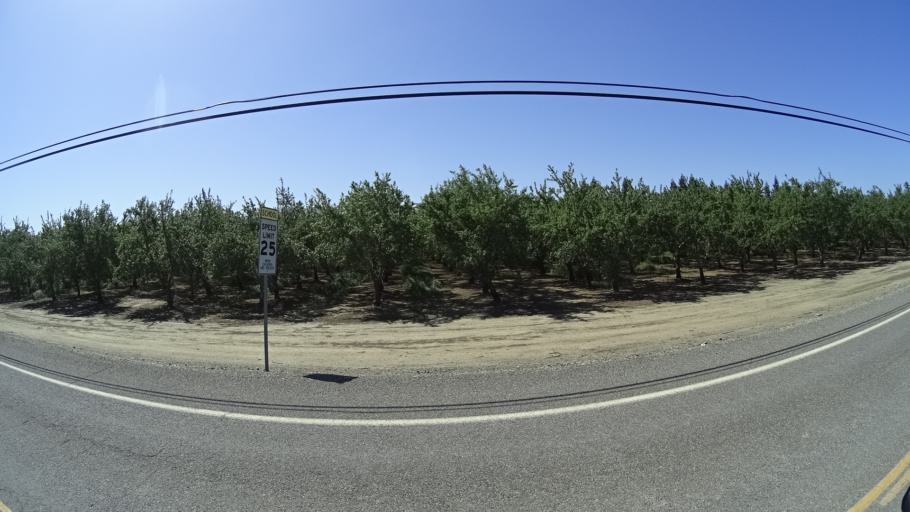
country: US
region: California
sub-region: Glenn County
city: Orland
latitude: 39.7104
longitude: -122.1078
